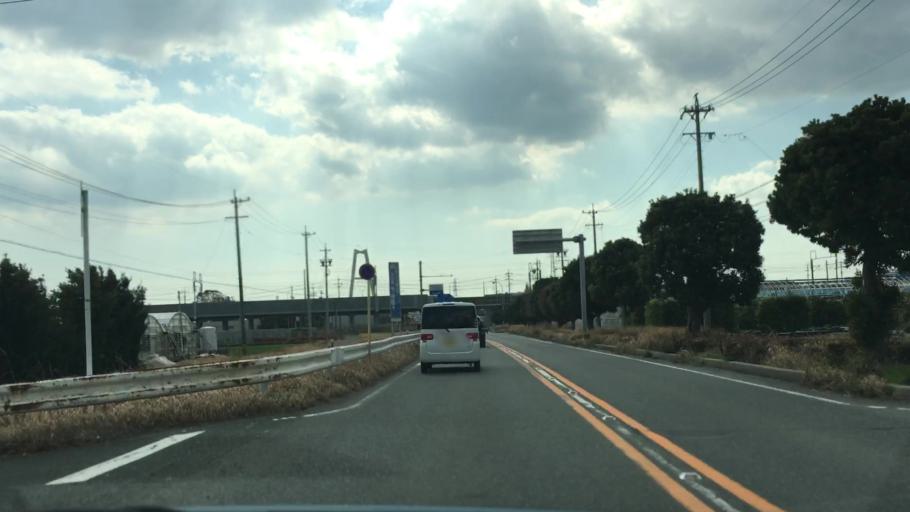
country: JP
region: Aichi
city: Kozakai-cho
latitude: 34.8104
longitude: 137.3093
